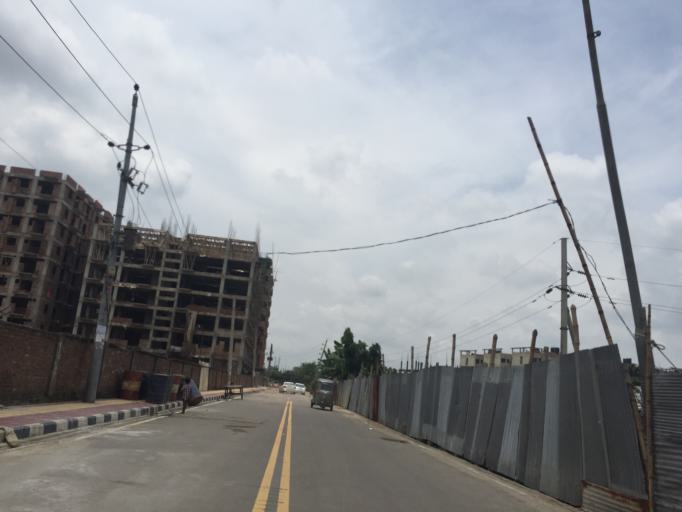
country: BD
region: Dhaka
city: Paltan
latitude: 23.8044
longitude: 90.3849
